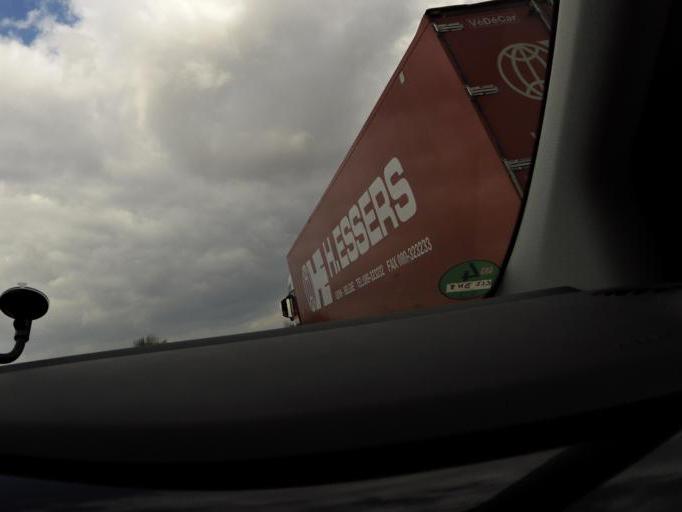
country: DE
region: North Rhine-Westphalia
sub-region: Regierungsbezirk Koln
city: Rheinbach
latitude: 50.6870
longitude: 6.9092
